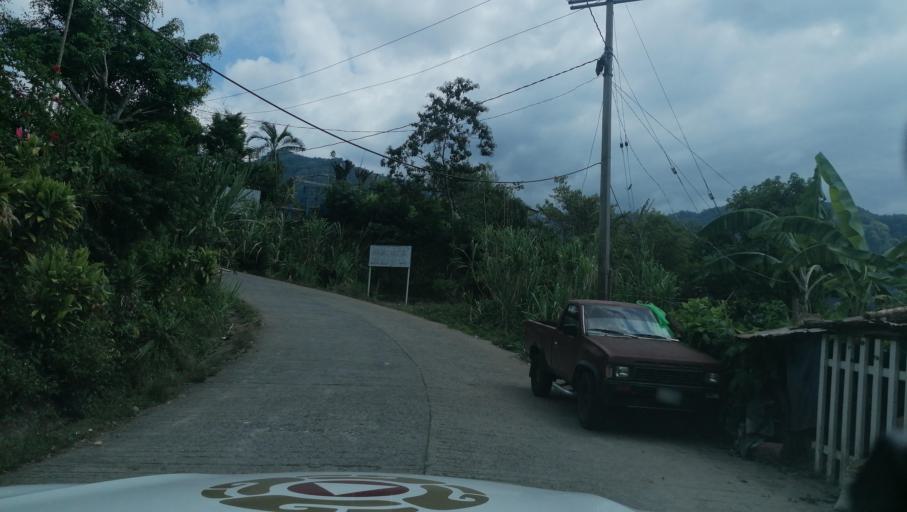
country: MX
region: Chiapas
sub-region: Cacahoatan
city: Benito Juarez
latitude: 15.1142
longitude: -92.2097
